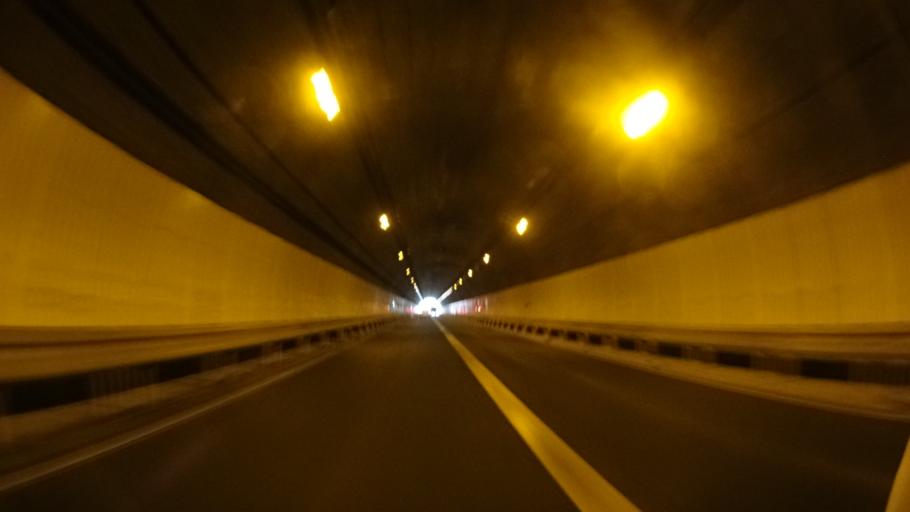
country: JP
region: Kagoshima
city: Kagoshima-shi
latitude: 31.6146
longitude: 130.5712
